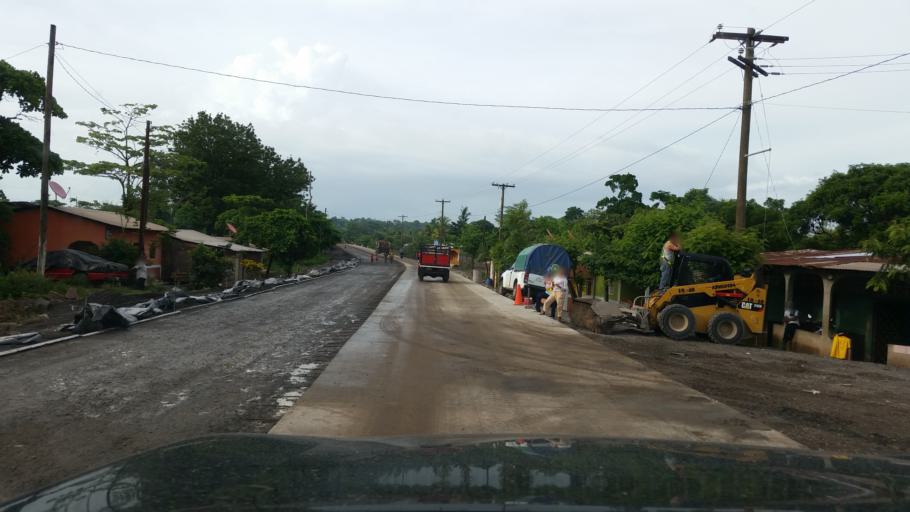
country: NI
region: Matagalpa
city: Rio Blanco
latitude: 13.0737
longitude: -85.0620
